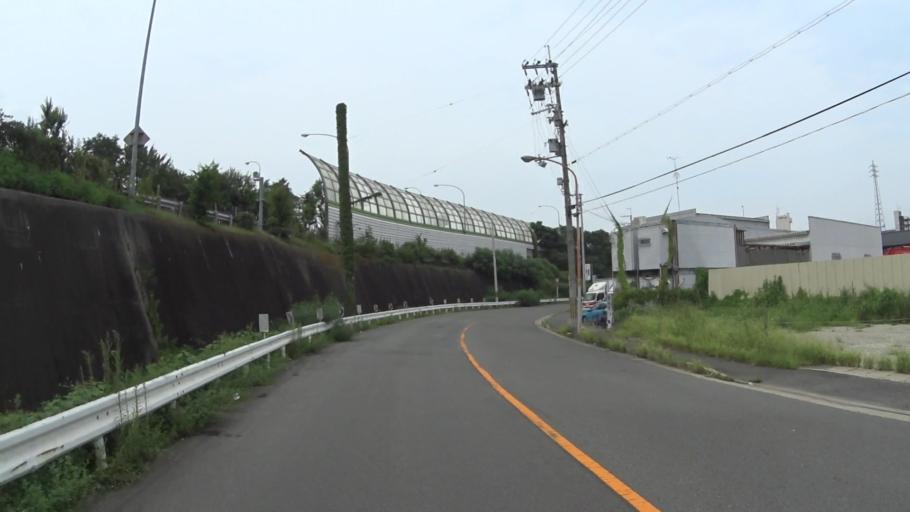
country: JP
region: Kyoto
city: Muko
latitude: 34.9543
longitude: 135.7482
